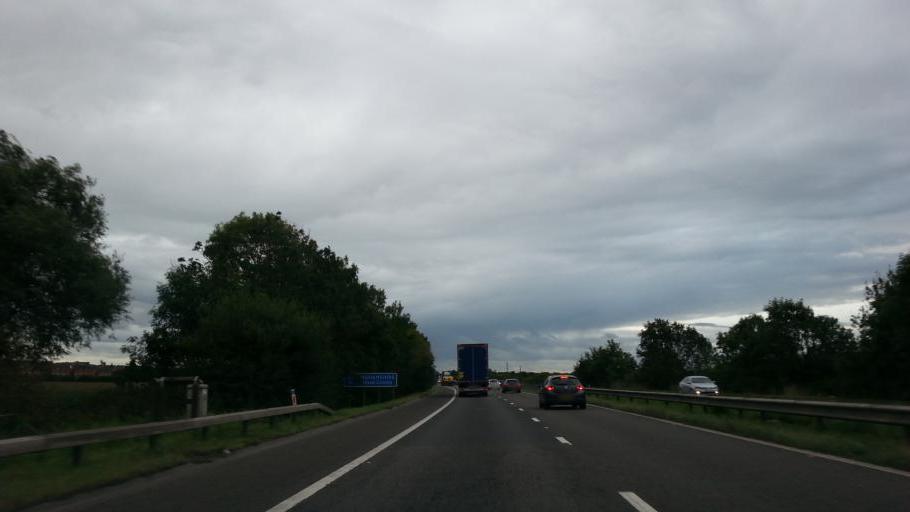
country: GB
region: England
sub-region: Doncaster
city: Tickhill
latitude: 53.4229
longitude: -1.0918
